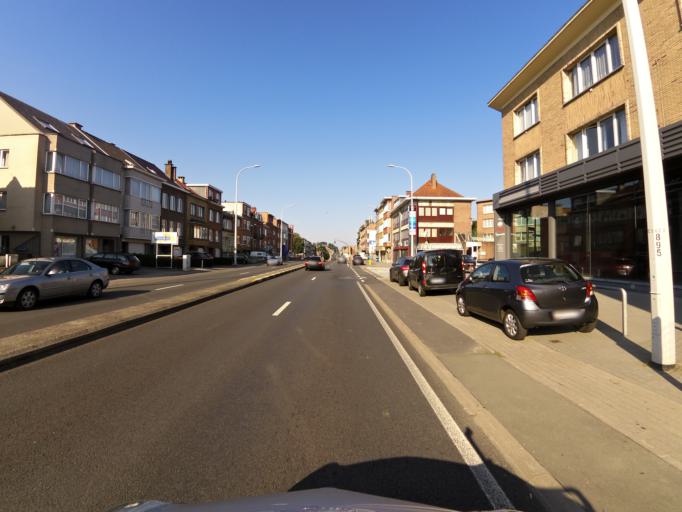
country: BE
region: Flanders
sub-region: Provincie Vlaams-Brabant
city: Dilbeek
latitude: 50.8446
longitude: 4.2714
